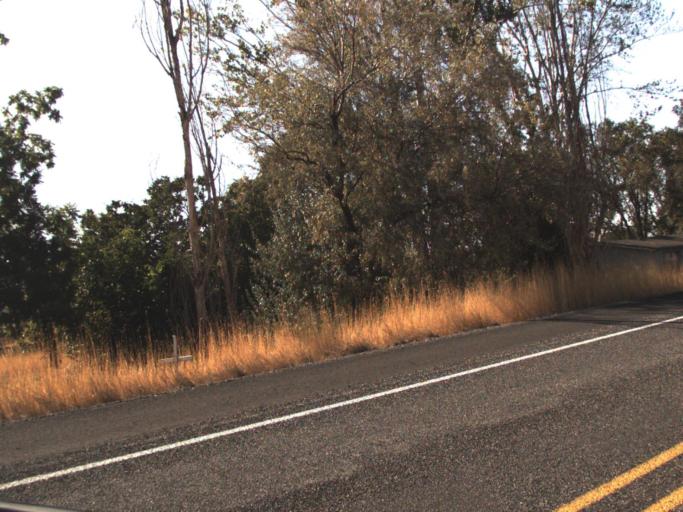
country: US
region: Washington
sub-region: Benton County
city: Finley
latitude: 46.1484
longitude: -119.0222
